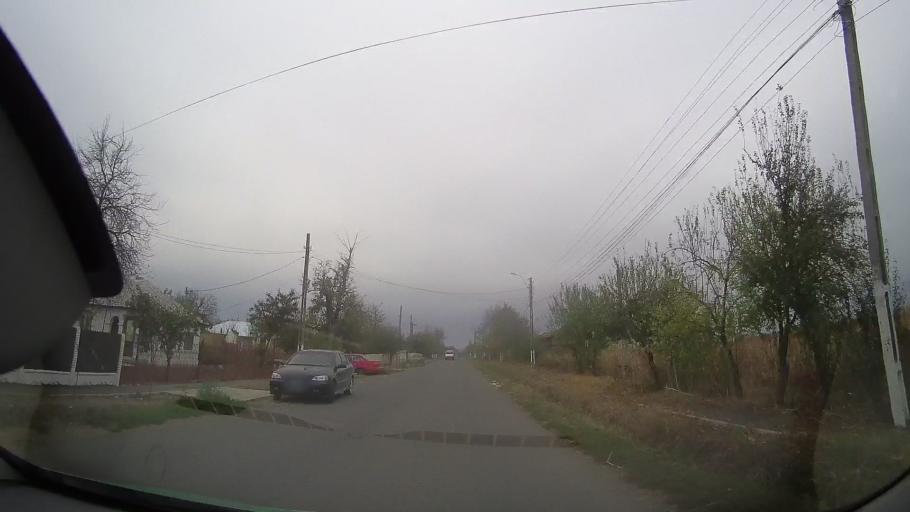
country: RO
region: Braila
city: Dudesti
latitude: 44.8747
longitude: 27.4302
